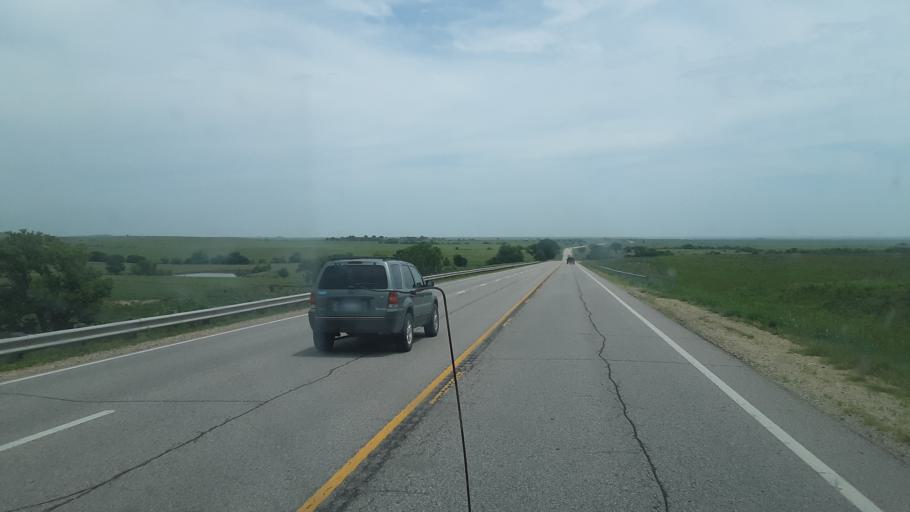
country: US
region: Kansas
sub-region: Greenwood County
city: Eureka
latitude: 37.8101
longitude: -96.5381
